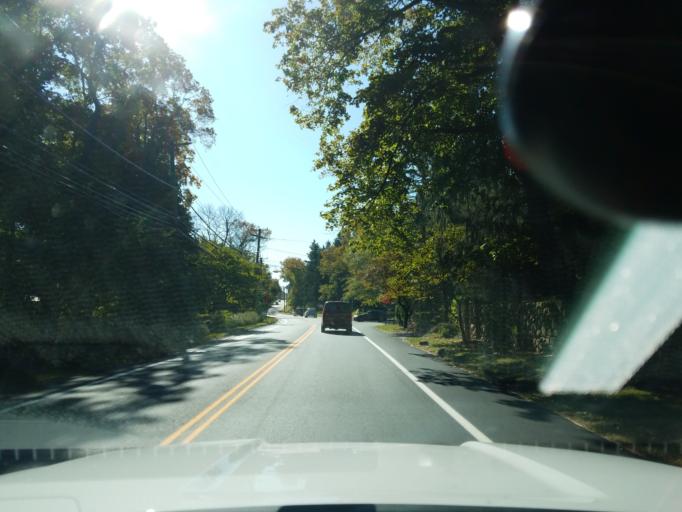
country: US
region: Connecticut
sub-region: Fairfield County
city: Cos Cob
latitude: 41.0715
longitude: -73.6231
